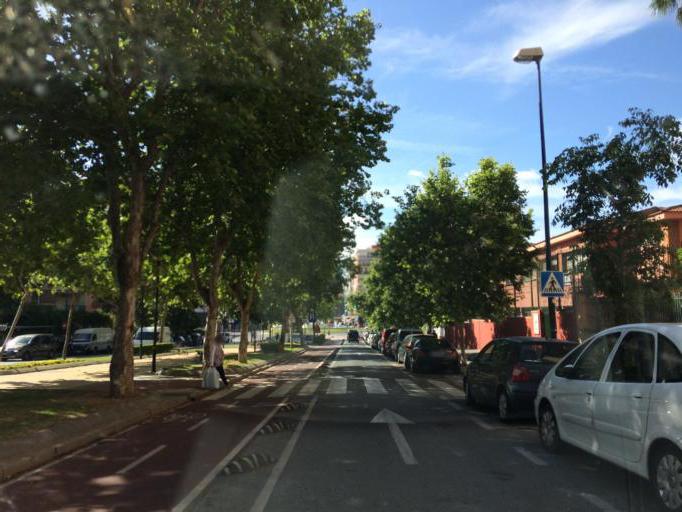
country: ES
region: Andalusia
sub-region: Provincia de Malaga
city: Malaga
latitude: 36.7133
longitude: -4.4419
